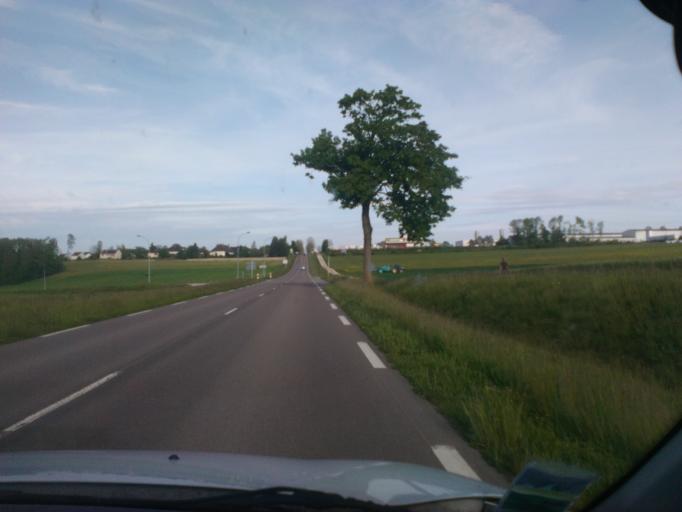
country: FR
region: Champagne-Ardenne
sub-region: Departement de l'Aube
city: Vendeuvre-sur-Barse
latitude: 48.2383
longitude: 4.4883
